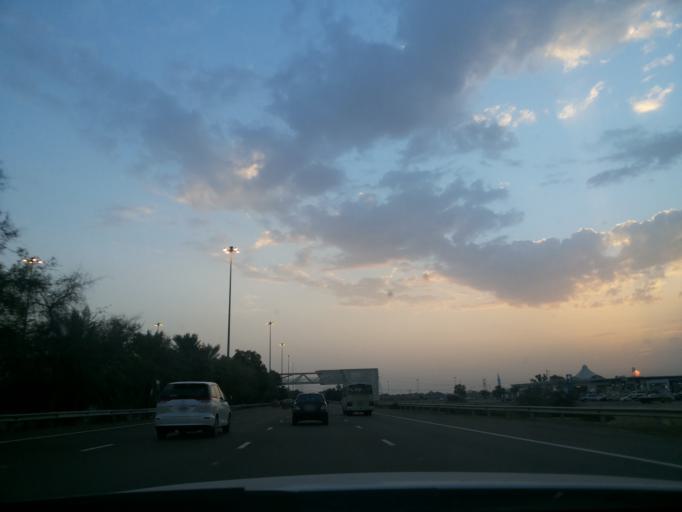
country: AE
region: Abu Dhabi
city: Abu Dhabi
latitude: 24.6716
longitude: 54.7616
